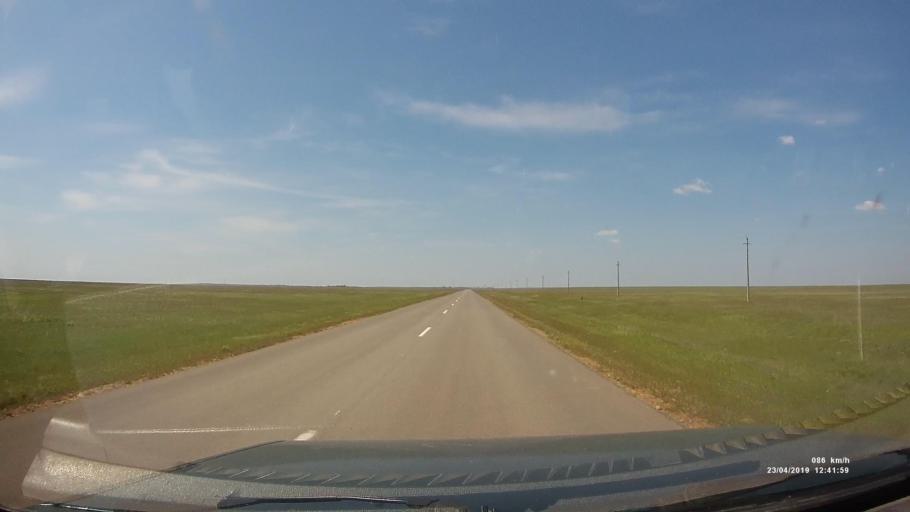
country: RU
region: Kalmykiya
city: Yashalta
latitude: 46.4524
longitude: 42.6726
